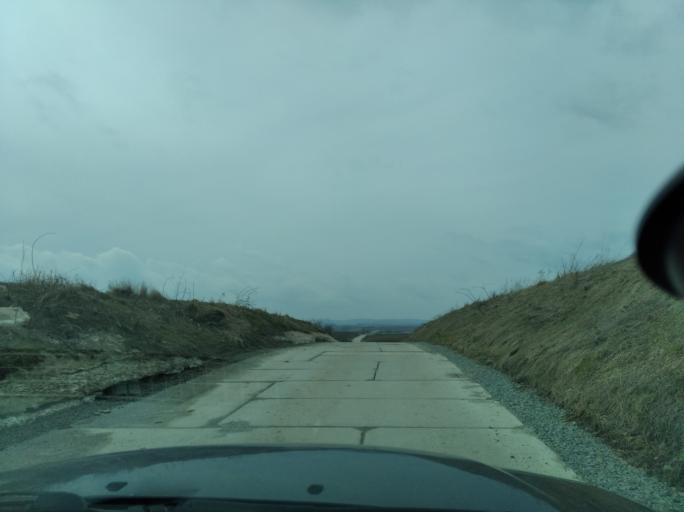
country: PL
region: Subcarpathian Voivodeship
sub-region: Powiat przeworski
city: Zarzecze
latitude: 49.9370
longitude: 22.5843
